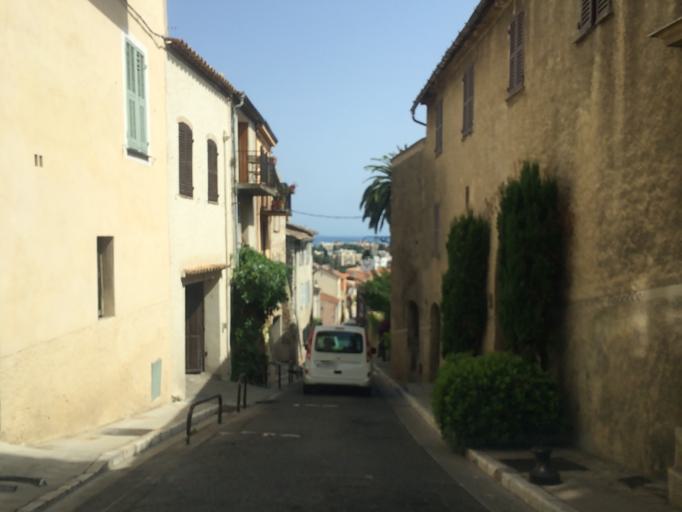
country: FR
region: Provence-Alpes-Cote d'Azur
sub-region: Departement des Alpes-Maritimes
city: Cagnes-sur-Mer
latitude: 43.6649
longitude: 7.1478
